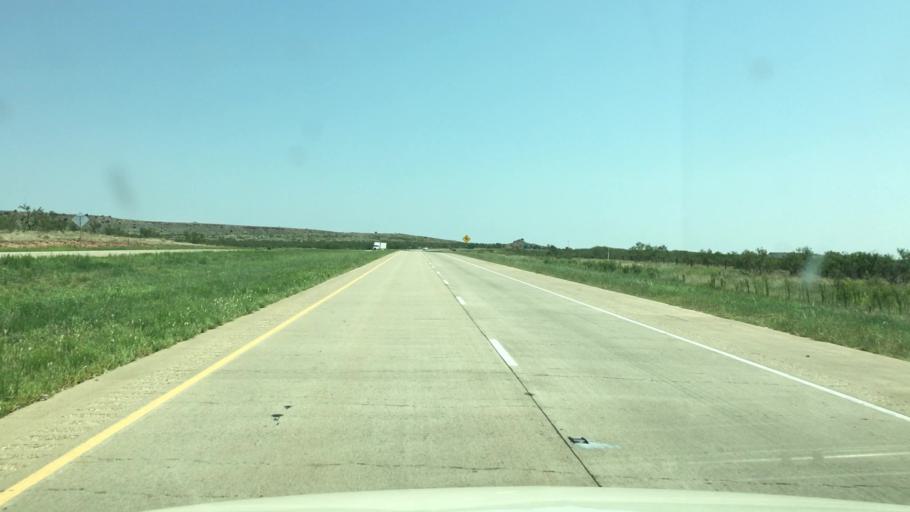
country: US
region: Texas
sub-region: Oldham County
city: Vega
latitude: 35.2430
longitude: -102.8207
